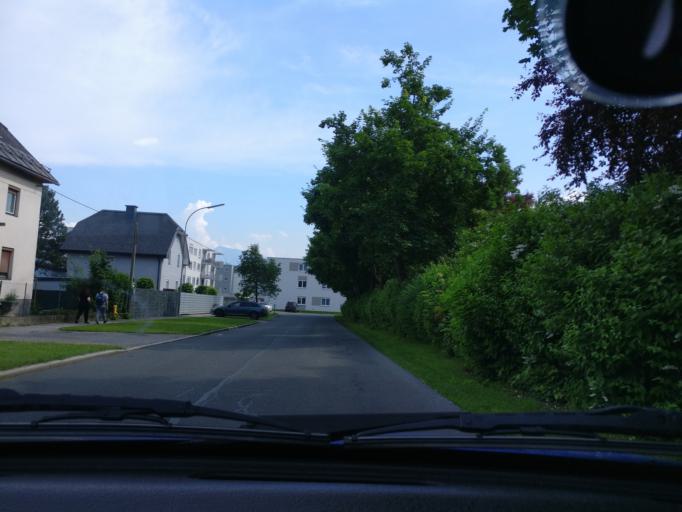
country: AT
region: Carinthia
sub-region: Klagenfurt am Woerthersee
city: Klagenfurt am Woerthersee
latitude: 46.6102
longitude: 14.2812
